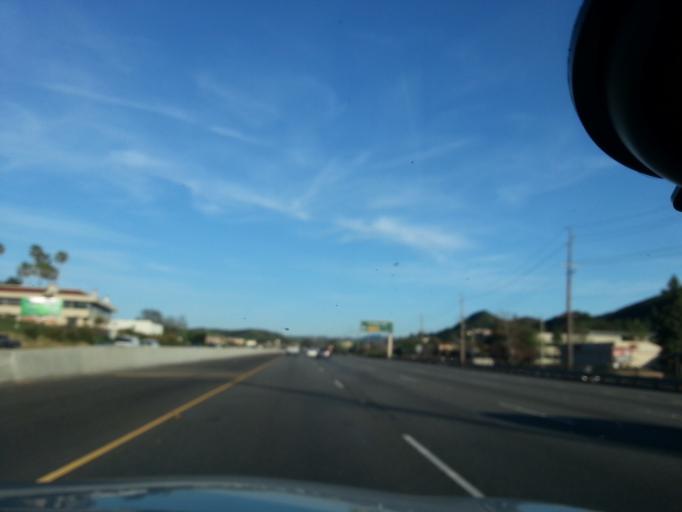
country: US
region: California
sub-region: Los Angeles County
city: Agoura
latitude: 34.1449
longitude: -118.7538
